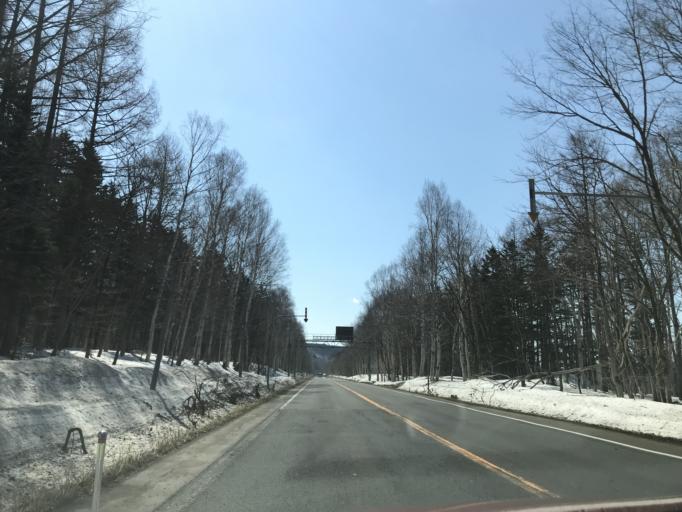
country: JP
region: Hokkaido
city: Nayoro
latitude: 44.7178
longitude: 142.2716
